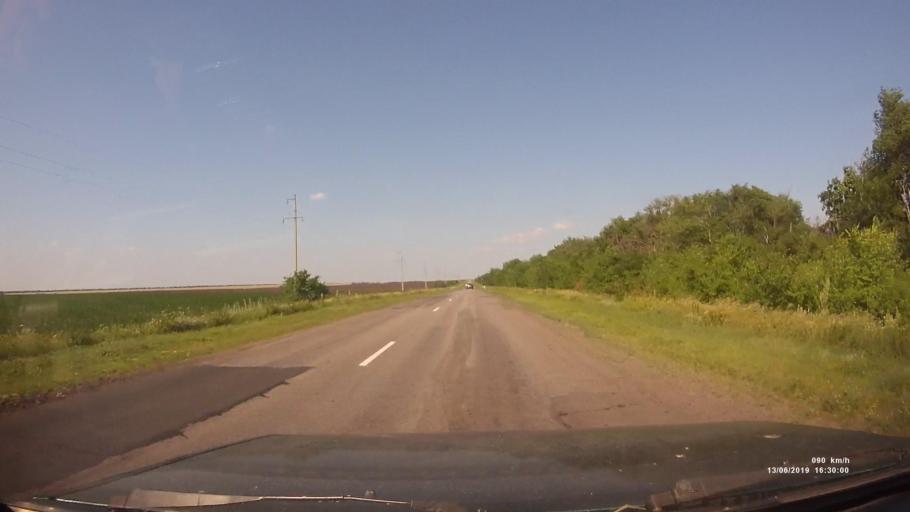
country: RU
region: Rostov
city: Kazanskaya
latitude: 49.8348
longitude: 41.2265
